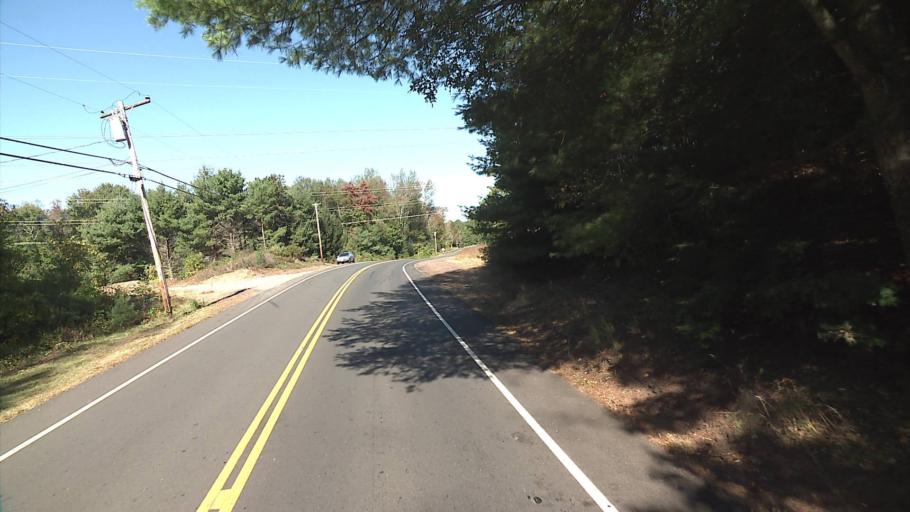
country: US
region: Connecticut
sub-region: Tolland County
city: Somers
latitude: 42.0211
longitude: -72.4507
